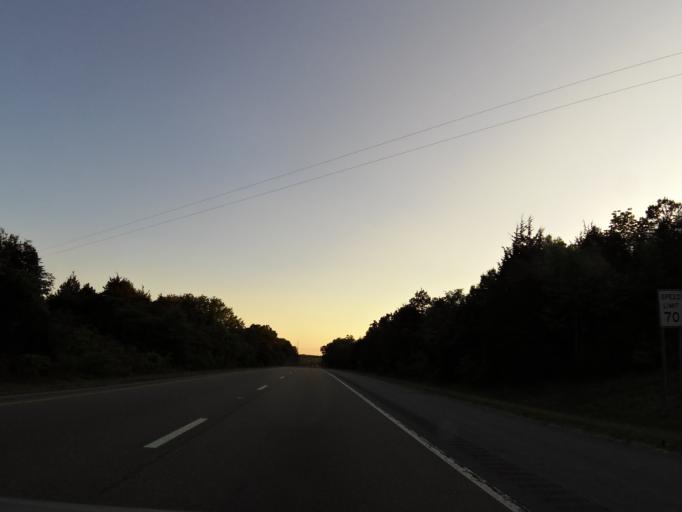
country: US
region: Tennessee
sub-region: Hawkins County
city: Surgoinsville
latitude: 36.3168
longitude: -82.8453
